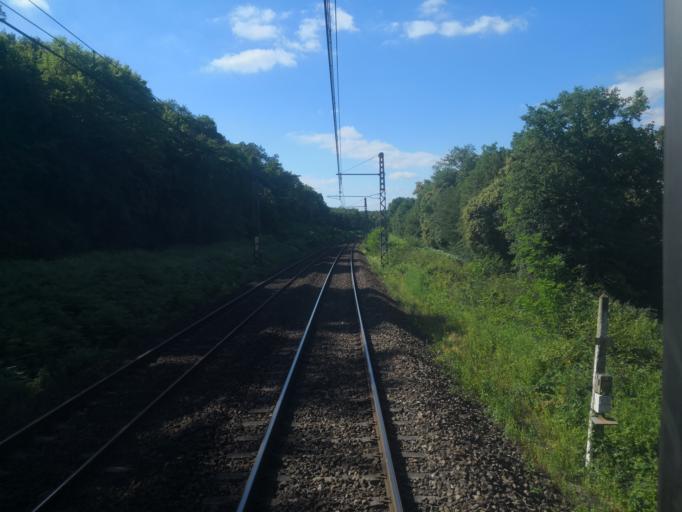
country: FR
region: Ile-de-France
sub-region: Departement de Seine-et-Marne
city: La Rochette
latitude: 48.4890
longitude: 2.6729
